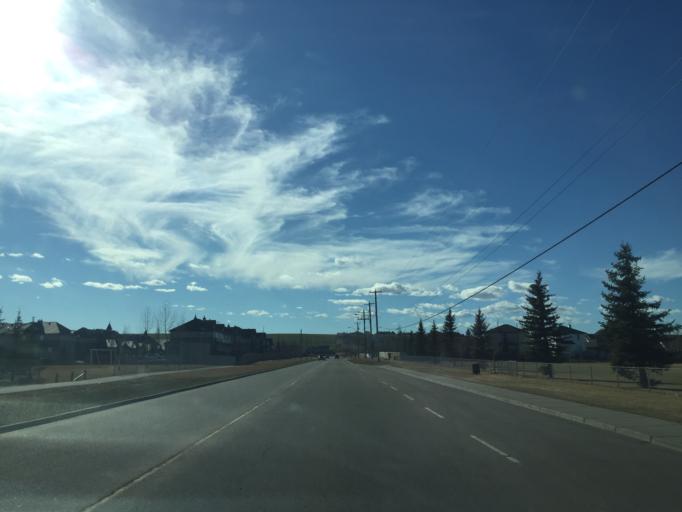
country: CA
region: Alberta
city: Airdrie
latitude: 51.2928
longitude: -114.0384
